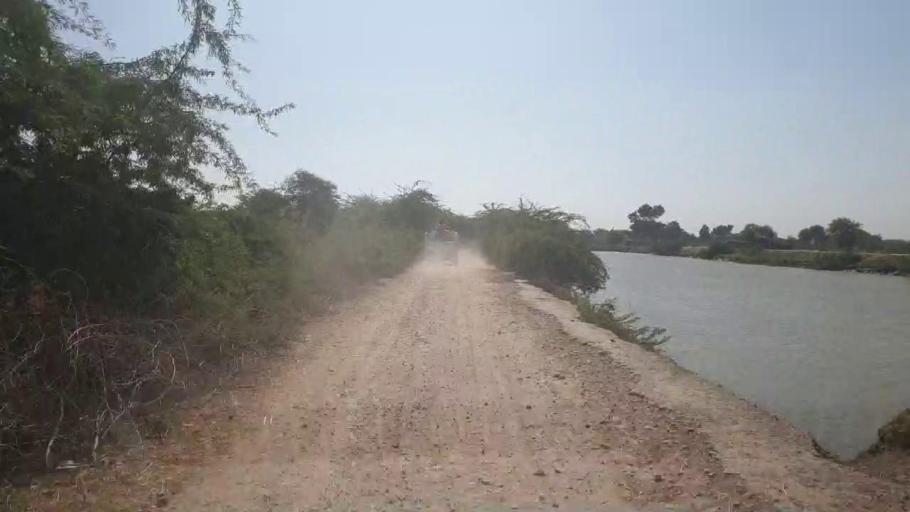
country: PK
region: Sindh
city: Talhar
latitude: 24.8316
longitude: 68.7955
